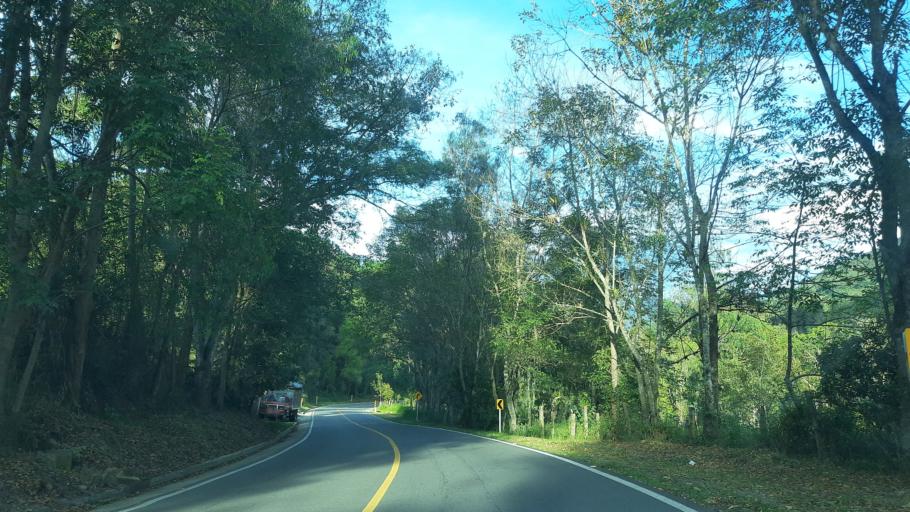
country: CO
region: Cundinamarca
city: Macheta
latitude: 5.0723
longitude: -73.5909
